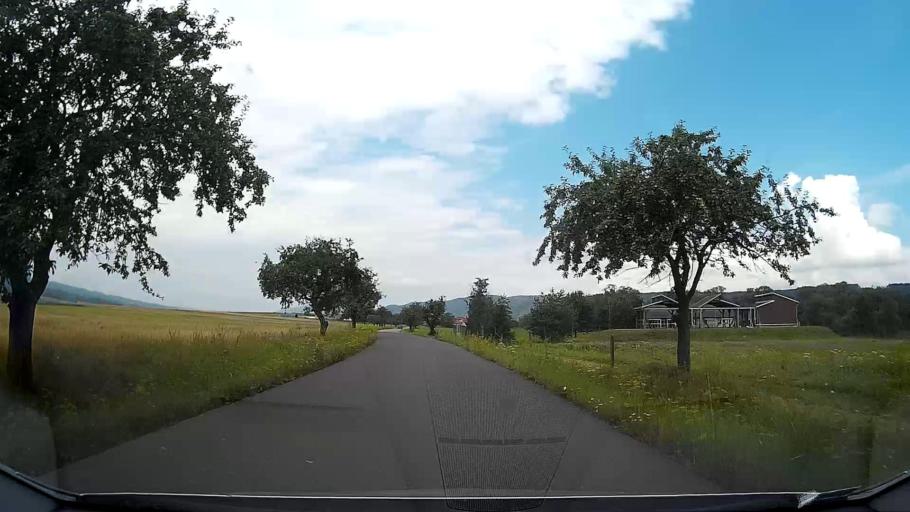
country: SK
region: Presovsky
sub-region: Okres Poprad
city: Poprad
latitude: 48.9869
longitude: 20.3724
